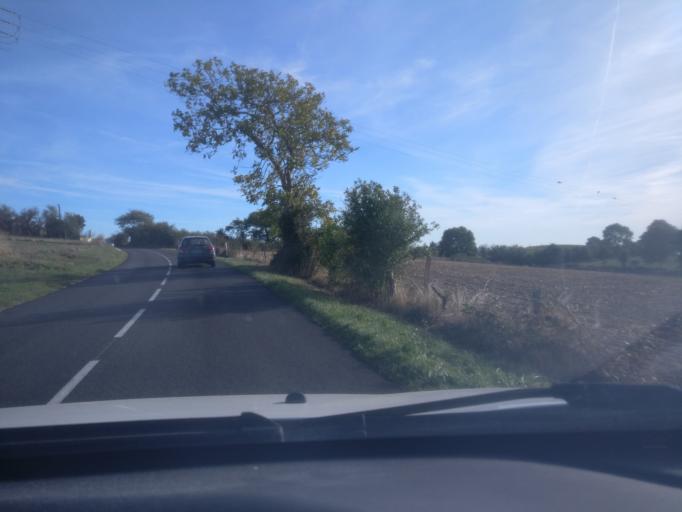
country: FR
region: Lower Normandy
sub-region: Departement de la Manche
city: Sartilly
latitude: 48.7221
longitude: -1.5070
